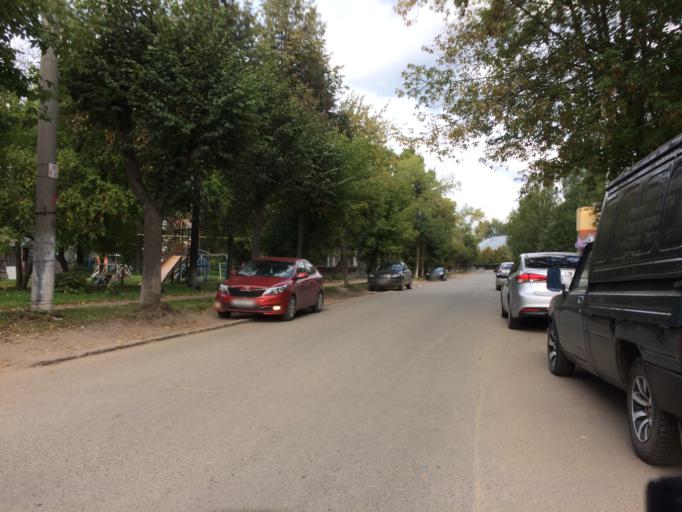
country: RU
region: Mariy-El
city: Yoshkar-Ola
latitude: 56.6371
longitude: 47.8741
